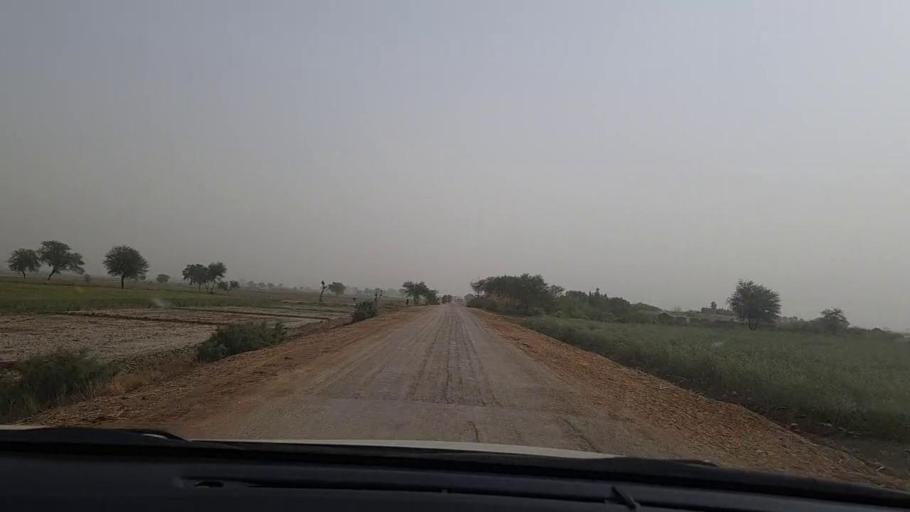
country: PK
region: Sindh
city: Pithoro
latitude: 25.4058
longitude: 69.3189
